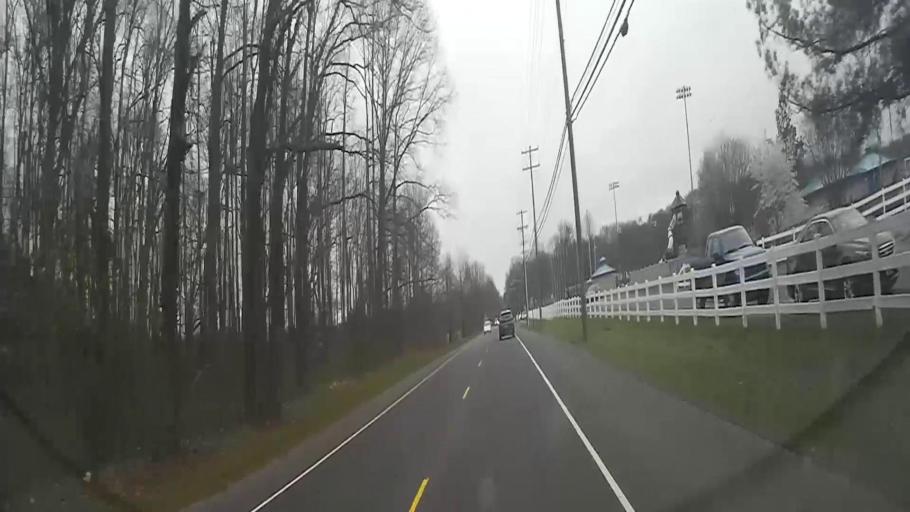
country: US
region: New Jersey
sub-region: Burlington County
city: Marlton
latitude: 39.8822
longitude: -74.8731
